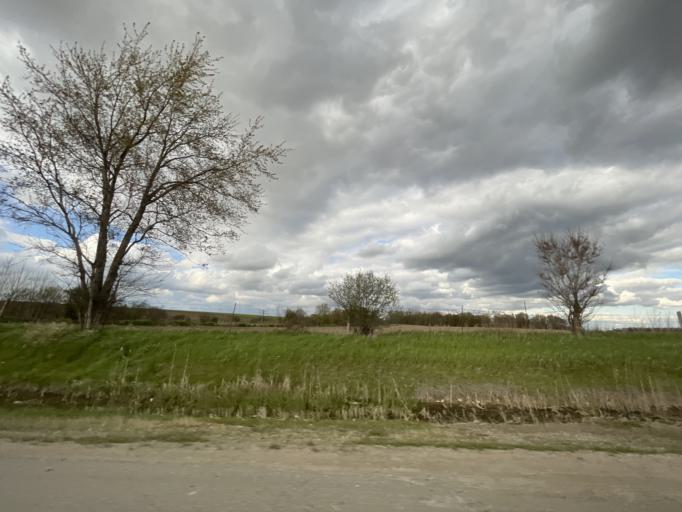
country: CA
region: Ontario
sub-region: Wellington County
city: Guelph
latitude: 43.5149
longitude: -80.3182
